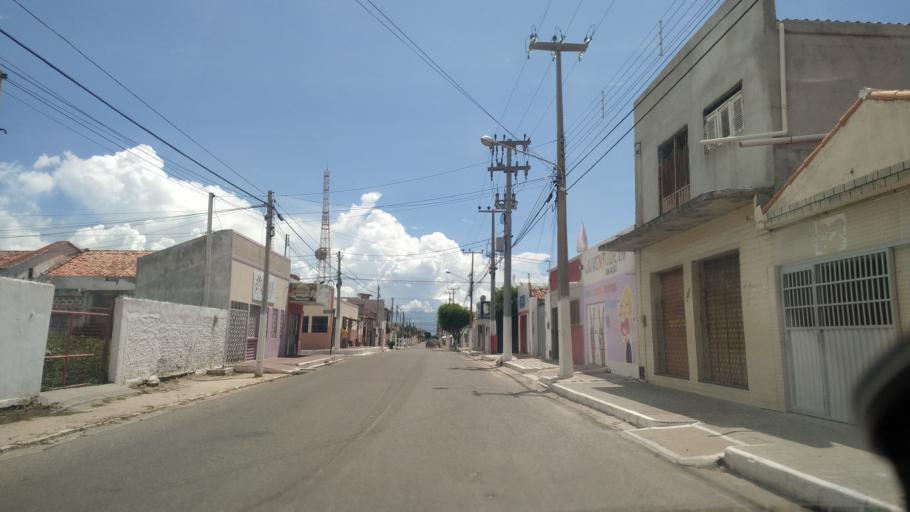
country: BR
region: Rio Grande do Norte
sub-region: Areia Branca
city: Areia Branca
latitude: -4.9543
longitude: -37.1323
